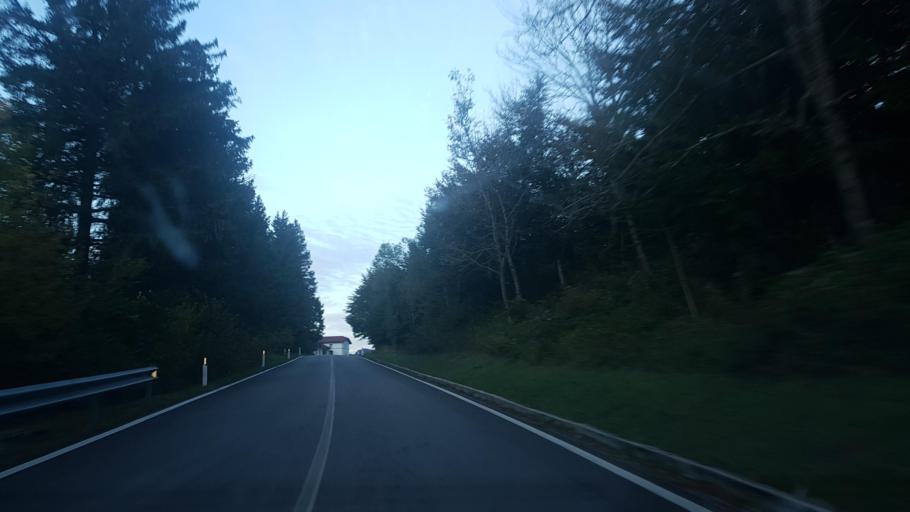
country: IT
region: Friuli Venezia Giulia
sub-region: Provincia di Udine
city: Chiaulis
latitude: 46.3603
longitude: 12.9429
